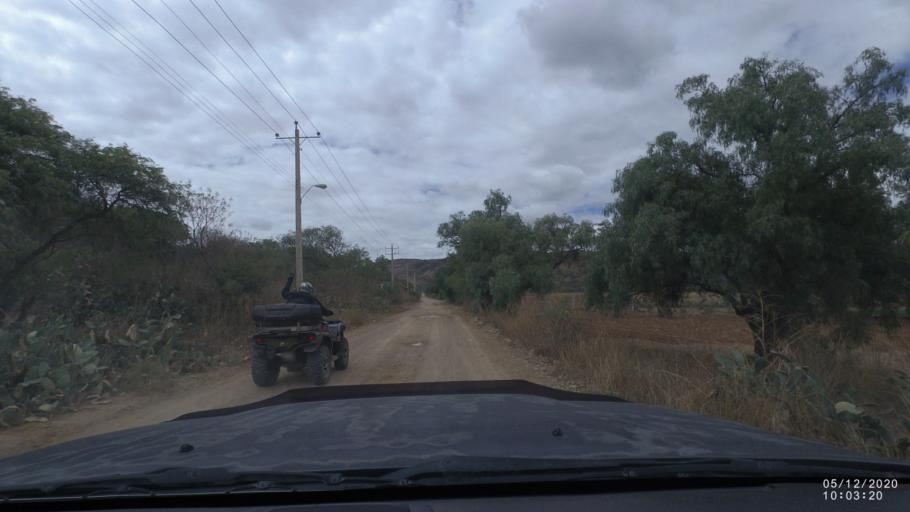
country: BO
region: Cochabamba
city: Sipe Sipe
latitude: -17.4567
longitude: -66.2867
